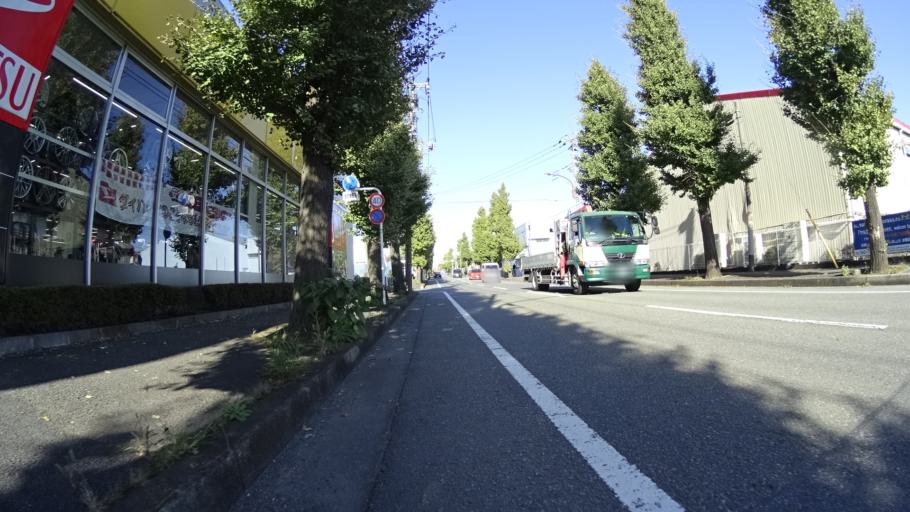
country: JP
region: Kanagawa
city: Zama
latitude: 35.5733
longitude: 139.3595
